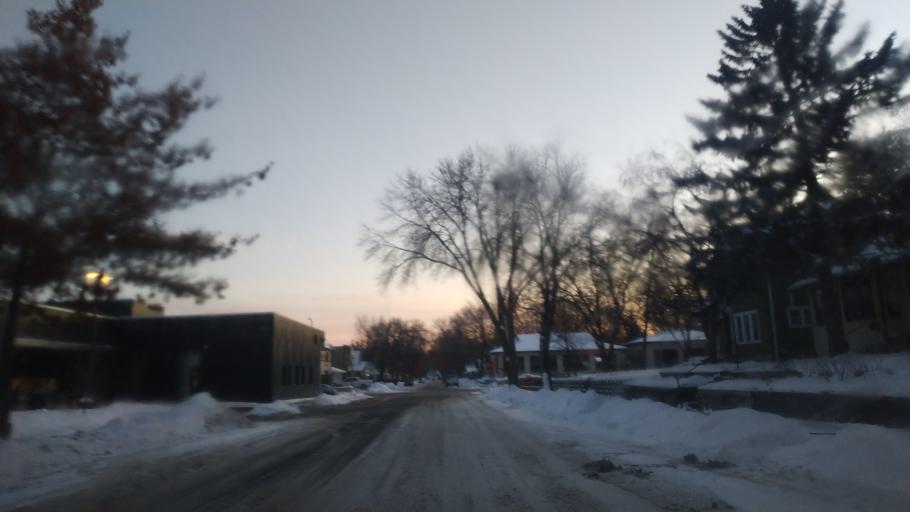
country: US
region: Minnesota
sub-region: Dakota County
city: South Saint Paul
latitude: 44.8896
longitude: -93.0463
